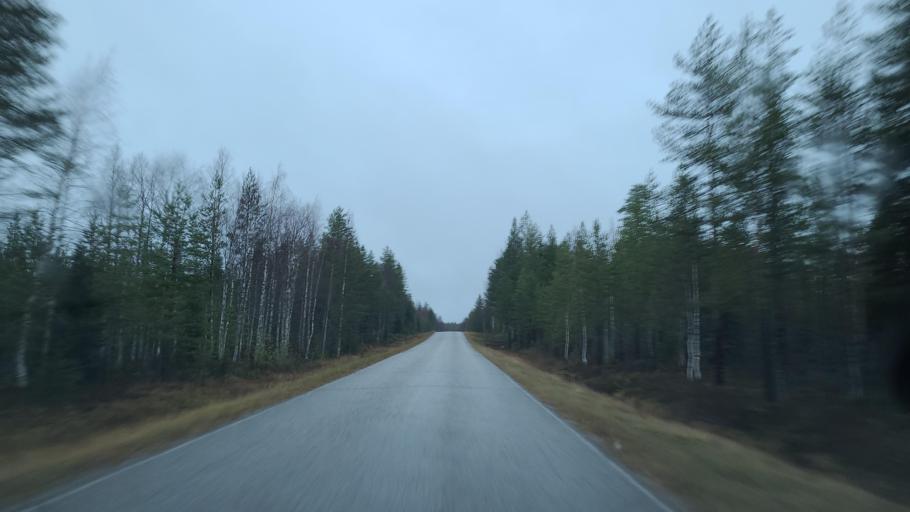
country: FI
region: Lapland
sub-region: Kemi-Tornio
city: Simo
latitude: 65.8953
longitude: 25.2122
